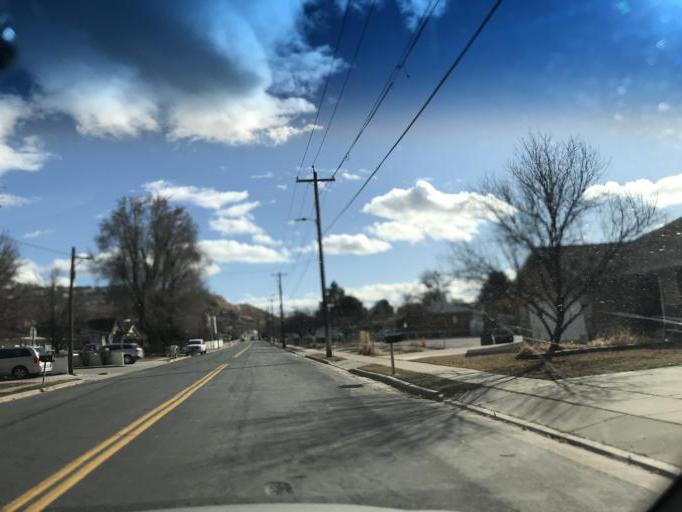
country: US
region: Utah
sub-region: Davis County
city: North Salt Lake
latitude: 40.8442
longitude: -111.9118
